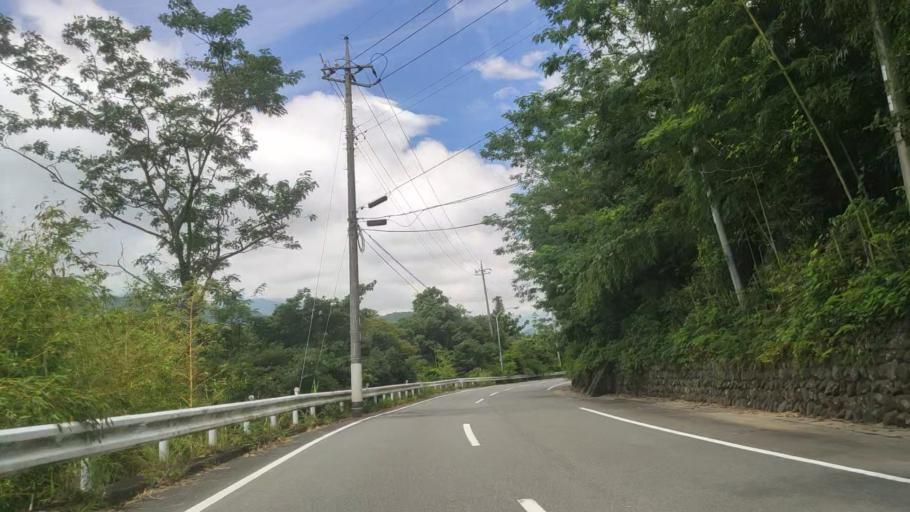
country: JP
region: Shizuoka
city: Fujinomiya
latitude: 35.2494
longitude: 138.4877
